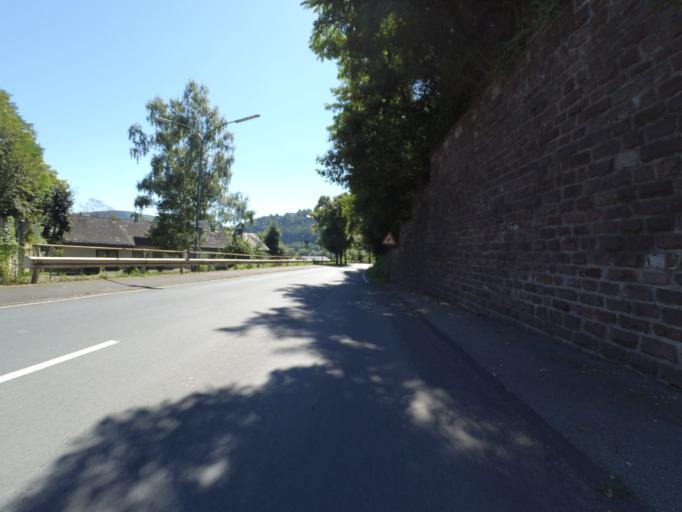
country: DE
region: Rheinland-Pfalz
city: Bullay
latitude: 50.0512
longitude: 7.1356
